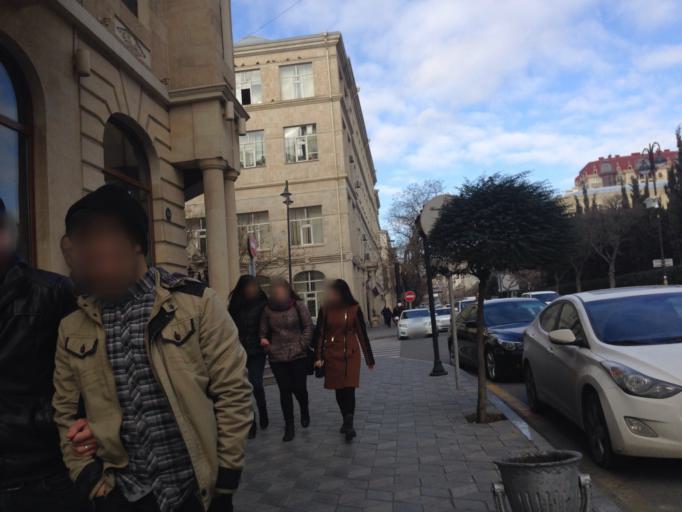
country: AZ
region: Baki
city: Baku
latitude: 40.3748
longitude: 49.8498
